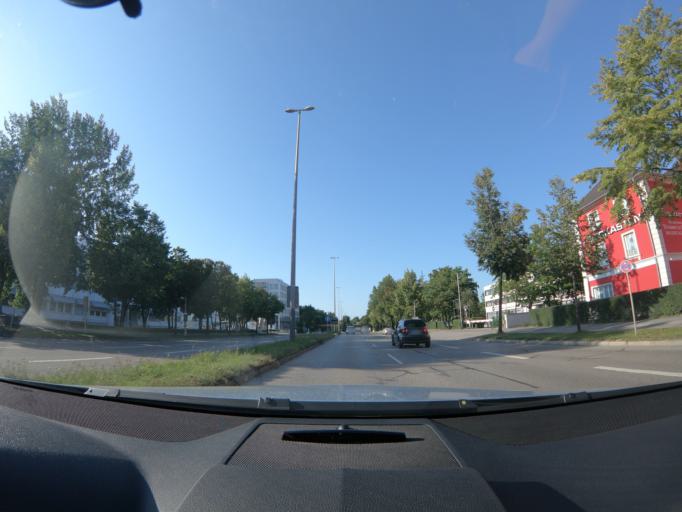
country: DE
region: Bavaria
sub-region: Upper Bavaria
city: Bogenhausen
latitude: 48.1887
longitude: 11.5845
